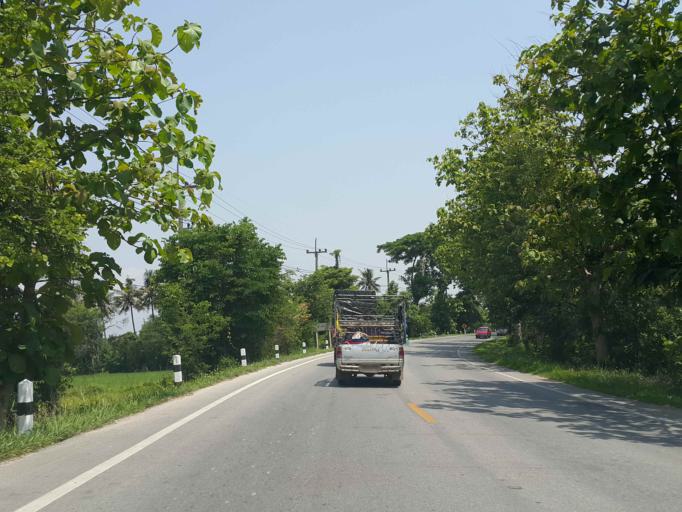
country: TH
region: Chiang Mai
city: Mae Taeng
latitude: 19.0022
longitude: 98.9724
